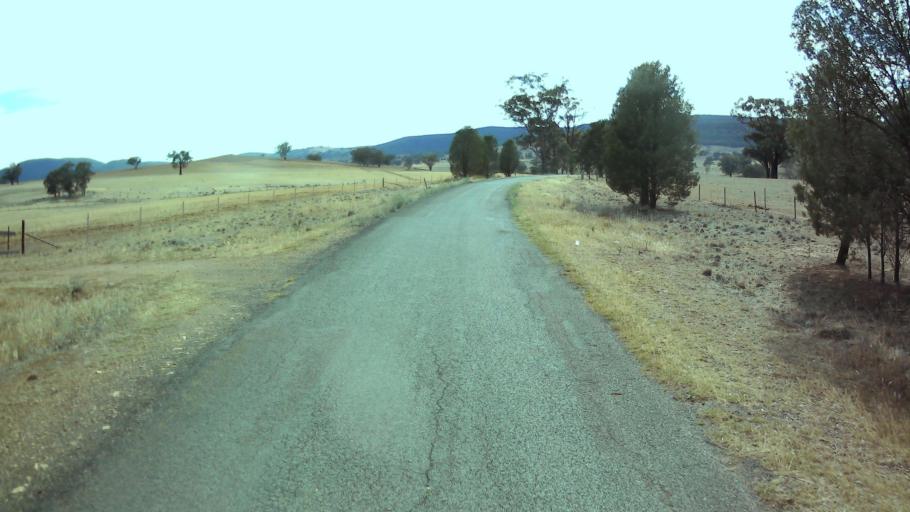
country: AU
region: New South Wales
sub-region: Weddin
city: Grenfell
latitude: -33.8294
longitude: 148.2788
